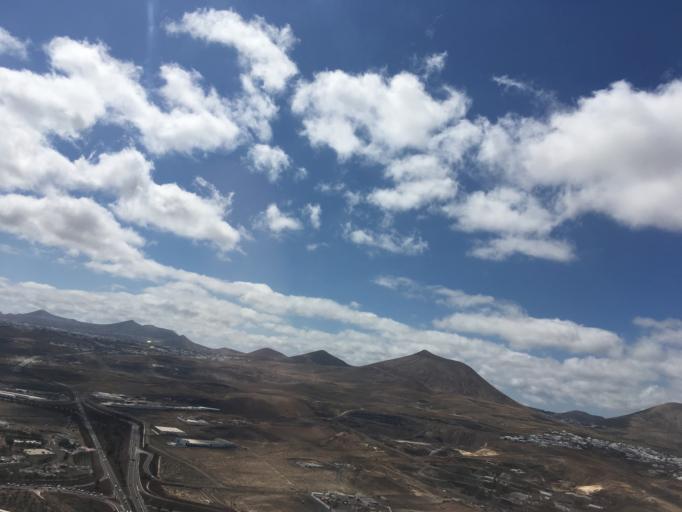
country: ES
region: Canary Islands
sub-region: Provincia de Las Palmas
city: Tias
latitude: 28.9552
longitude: -13.5981
